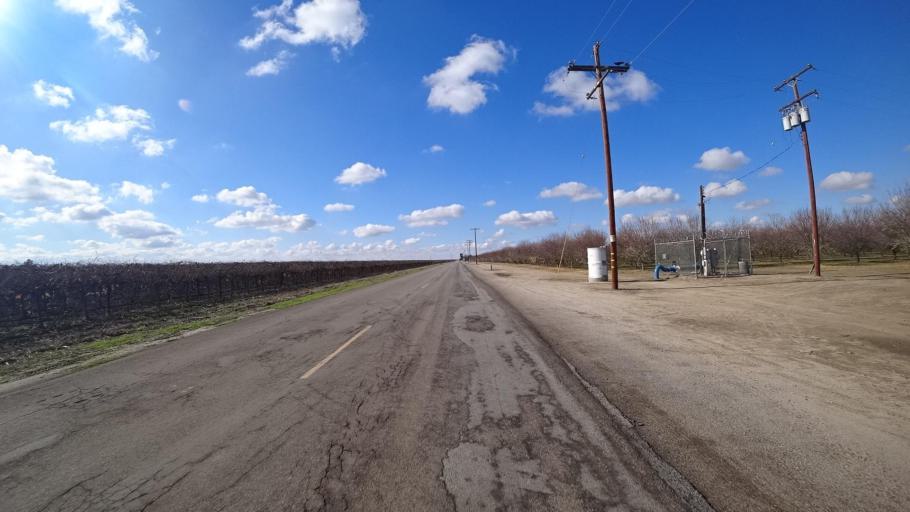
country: US
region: California
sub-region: Kern County
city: Delano
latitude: 35.7323
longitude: -119.2875
